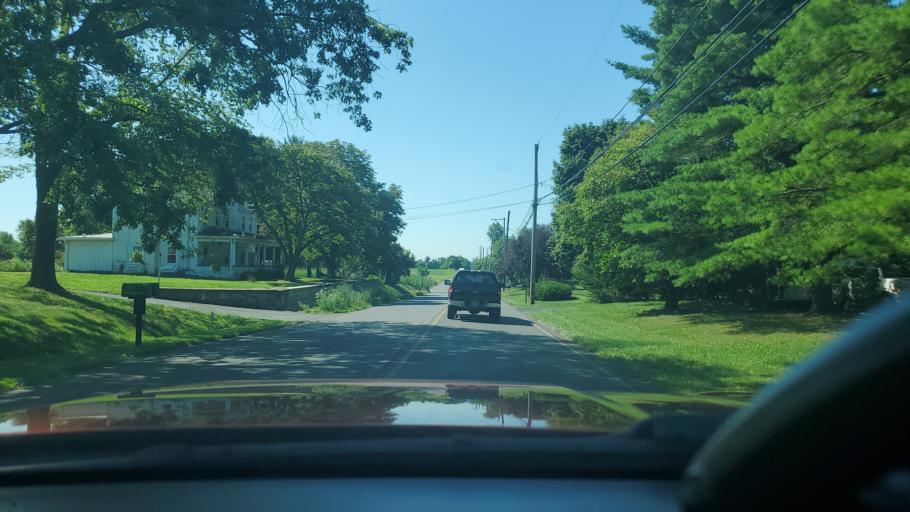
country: US
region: Pennsylvania
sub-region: Montgomery County
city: Limerick
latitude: 40.2403
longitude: -75.5282
